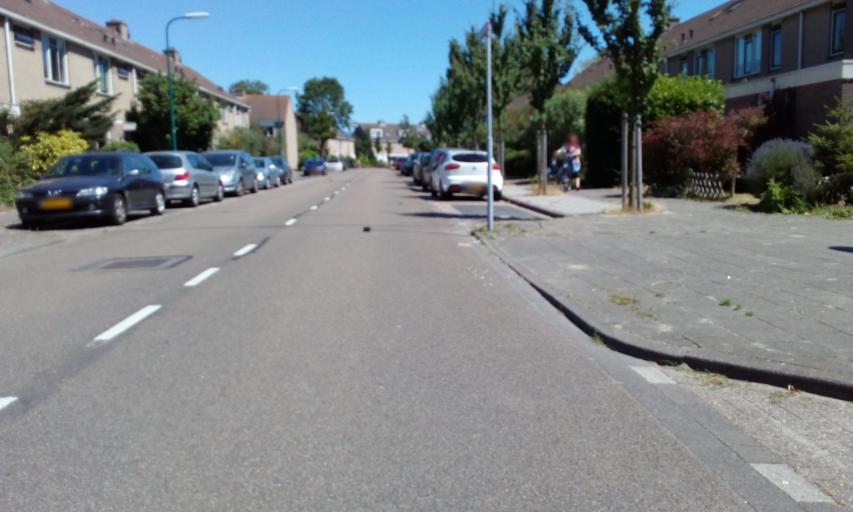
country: NL
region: South Holland
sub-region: Gemeente Oegstgeest
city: Oegstgeest
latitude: 52.1945
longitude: 4.4715
